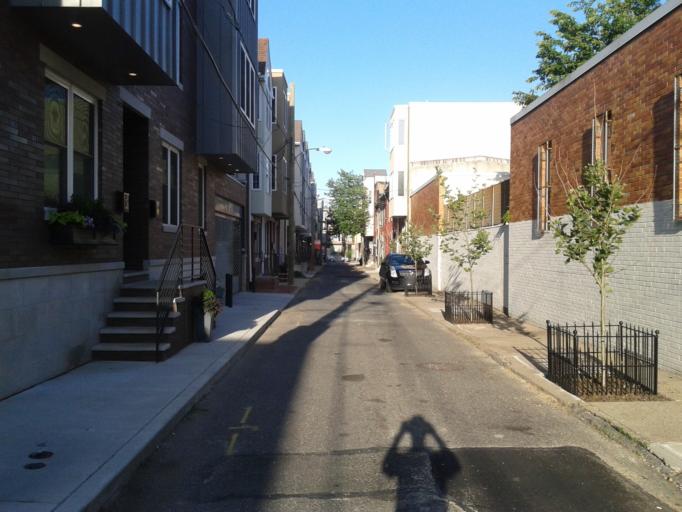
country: US
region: Pennsylvania
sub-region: Philadelphia County
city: Philadelphia
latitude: 39.9418
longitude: -75.1757
